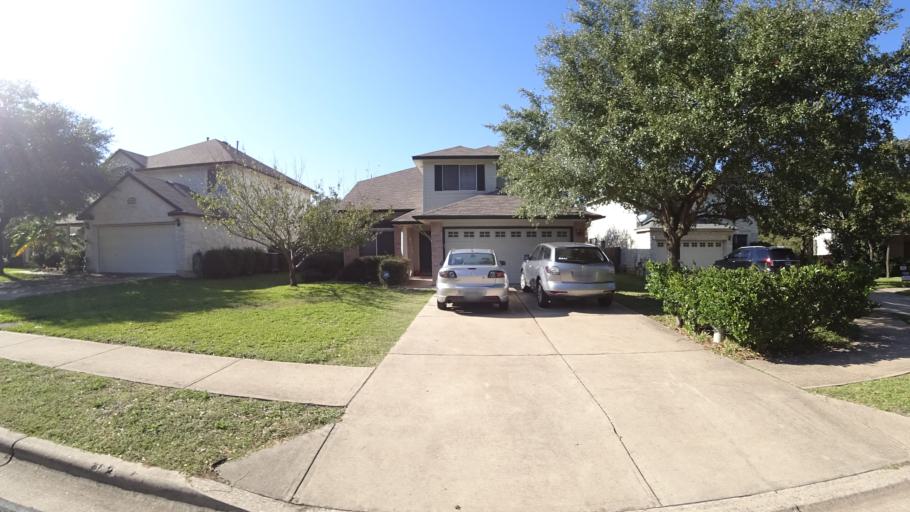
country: US
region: Texas
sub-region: Travis County
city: Shady Hollow
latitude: 30.2031
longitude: -97.8530
